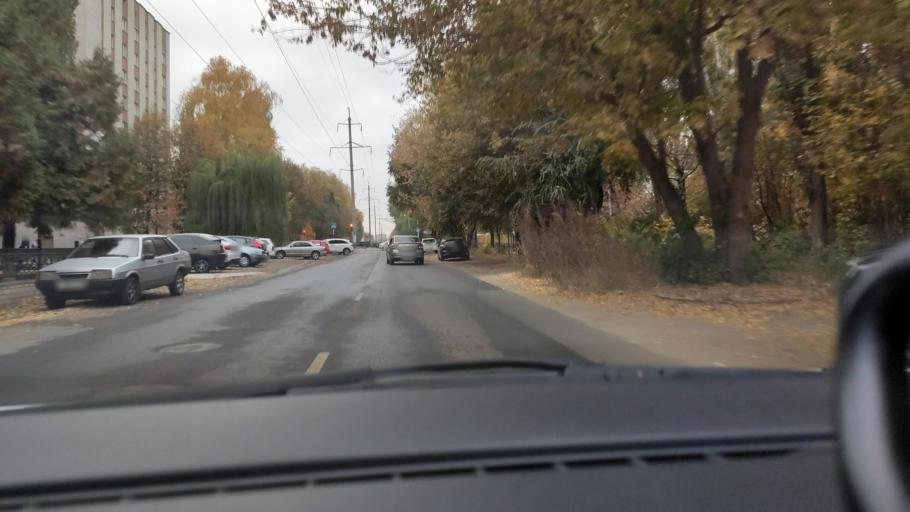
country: RU
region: Voronezj
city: Voronezh
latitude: 51.7155
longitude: 39.2289
